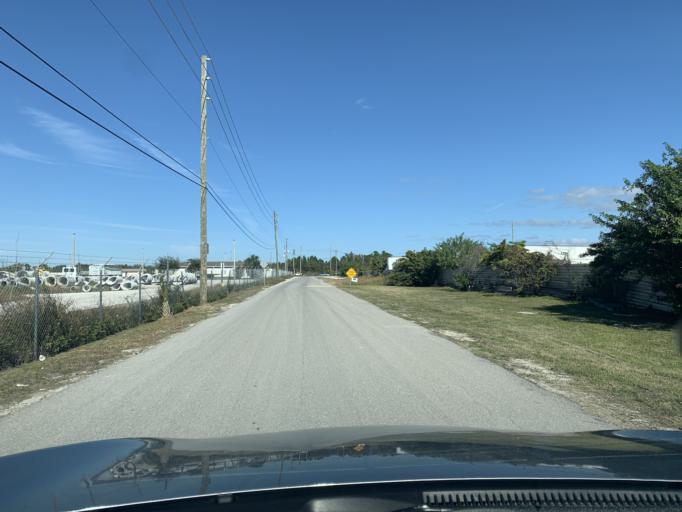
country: US
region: Florida
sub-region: Orange County
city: Lockhart
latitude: 28.6379
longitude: -81.4679
